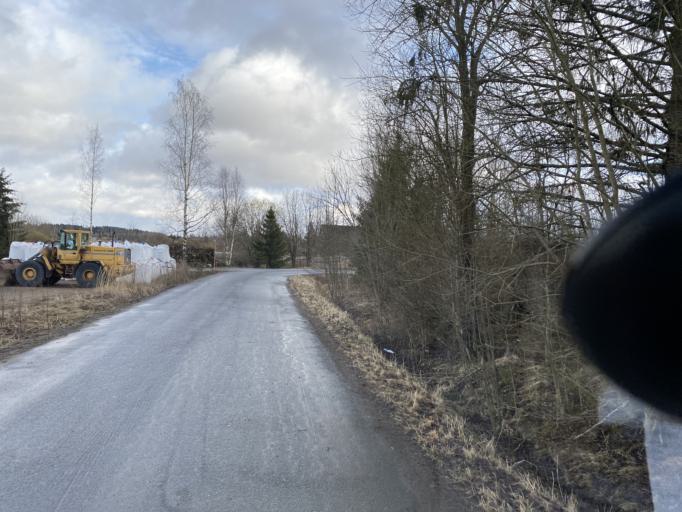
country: FI
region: Pirkanmaa
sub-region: Lounais-Pirkanmaa
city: Punkalaidun
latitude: 61.1213
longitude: 23.0915
